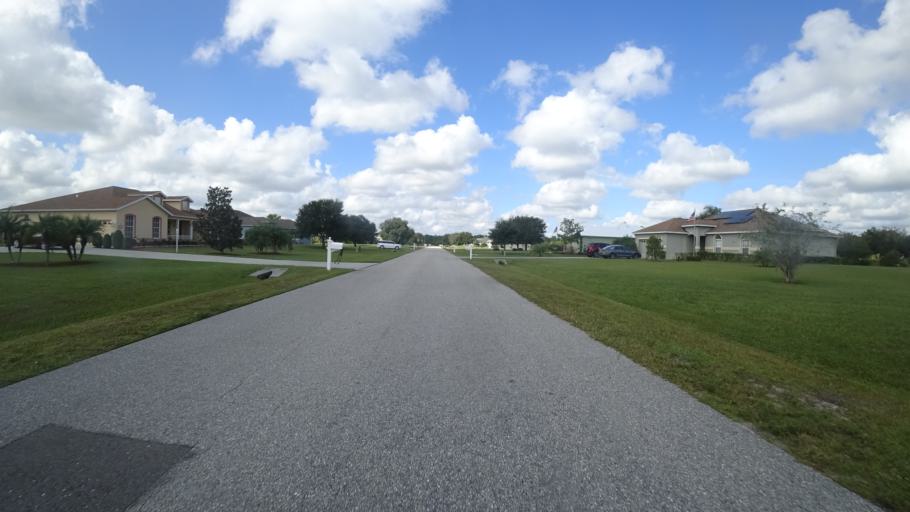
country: US
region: Florida
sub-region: Sarasota County
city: Lake Sarasota
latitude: 27.3966
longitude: -82.2722
